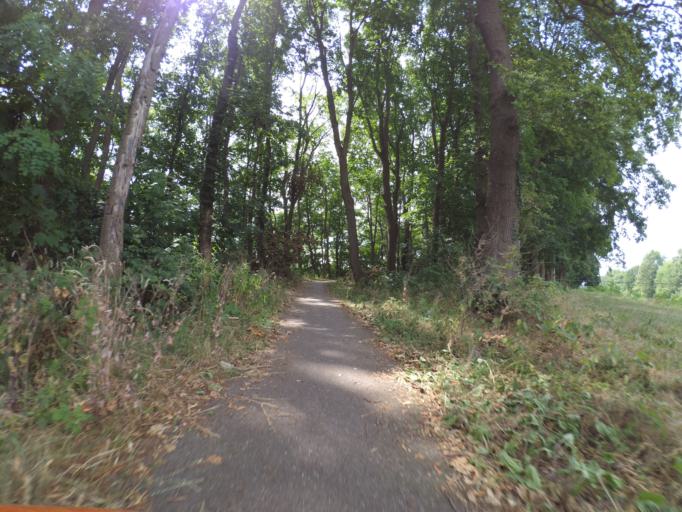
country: NL
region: Overijssel
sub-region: Gemeente Hof van Twente
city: Markelo
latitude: 52.1834
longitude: 6.4771
